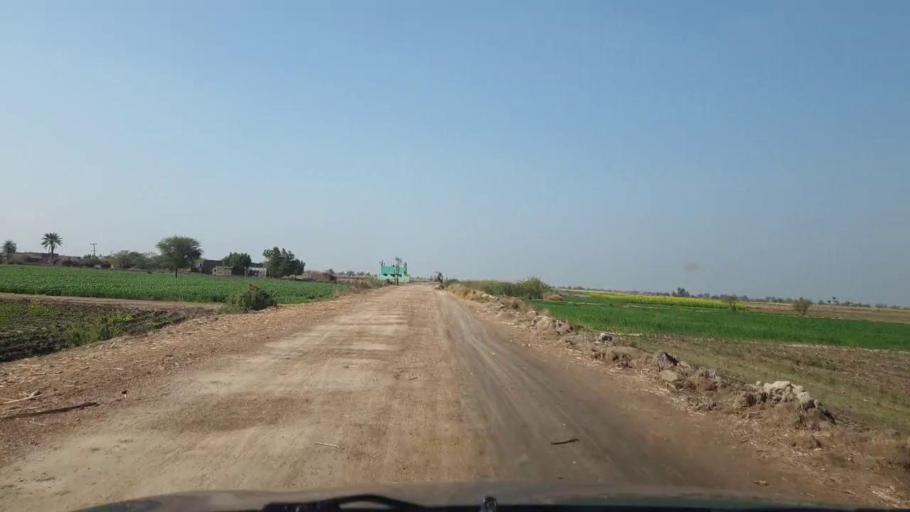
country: PK
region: Sindh
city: Sinjhoro
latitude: 26.0460
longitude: 68.7519
